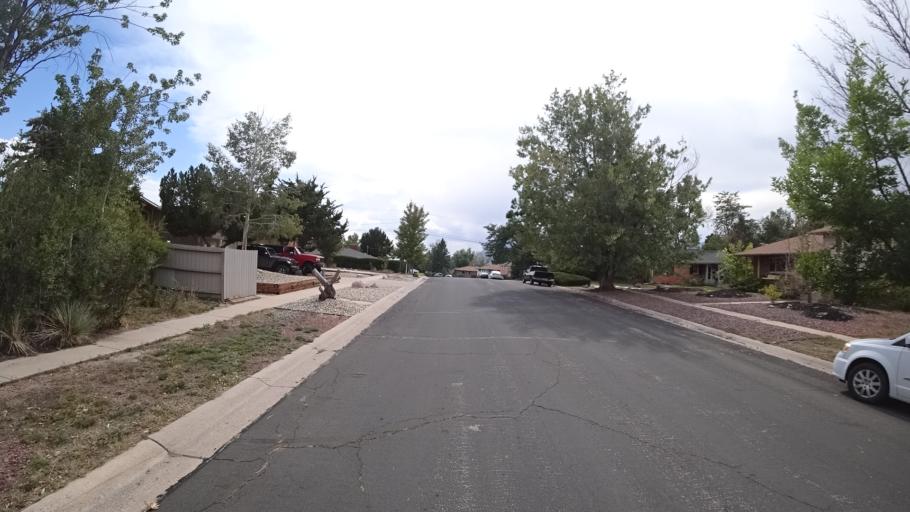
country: US
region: Colorado
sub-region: El Paso County
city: Colorado Springs
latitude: 38.8657
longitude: -104.7800
